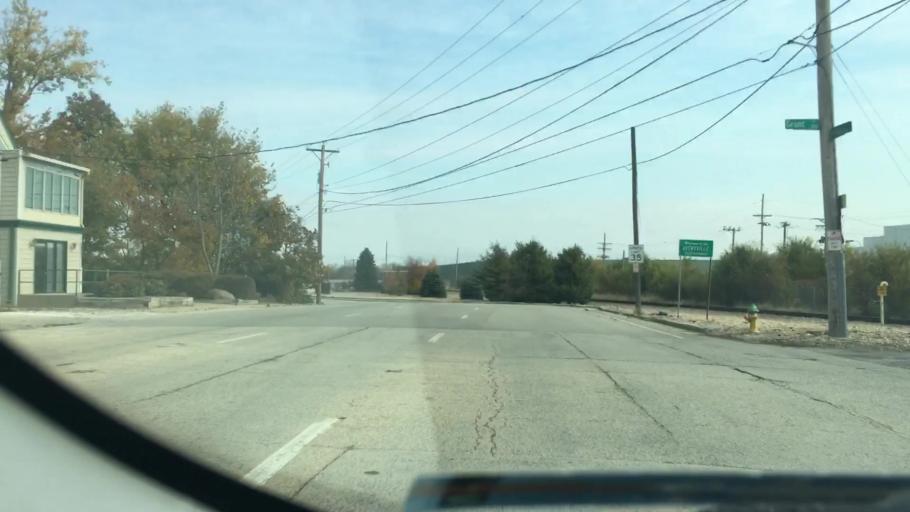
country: US
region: Illinois
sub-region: Peoria County
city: North Peoria
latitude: 40.7065
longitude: -89.5663
